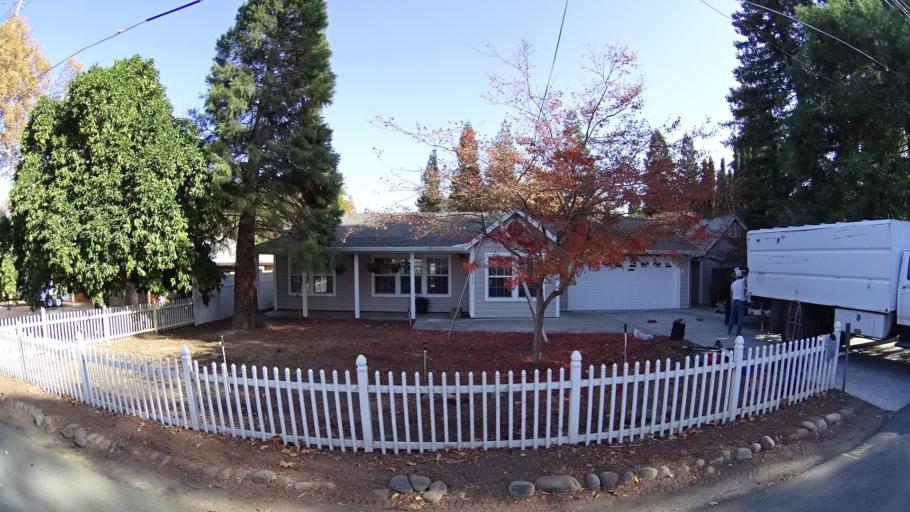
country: US
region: California
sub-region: Sacramento County
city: Citrus Heights
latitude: 38.7008
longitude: -121.2853
